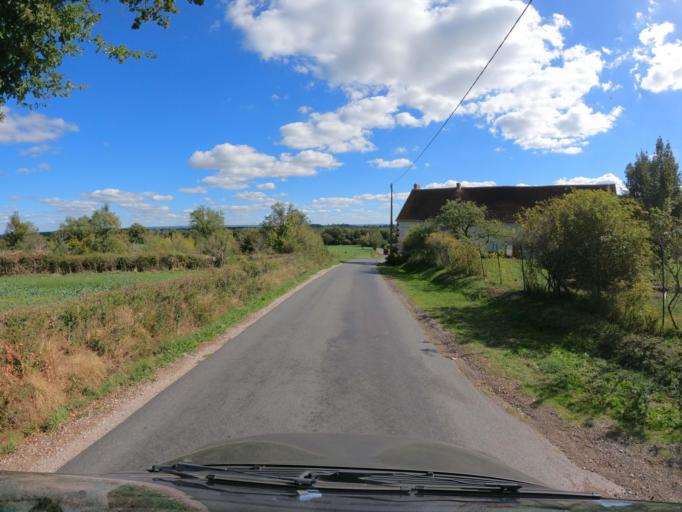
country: FR
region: Auvergne
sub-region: Departement de l'Allier
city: Doyet
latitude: 46.3978
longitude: 2.7505
